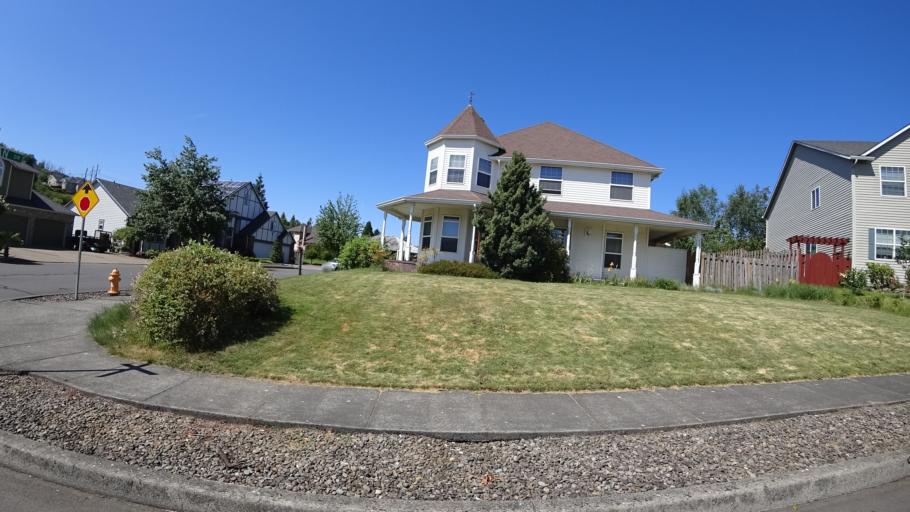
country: US
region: Oregon
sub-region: Multnomah County
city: Gresham
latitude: 45.4793
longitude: -122.4743
